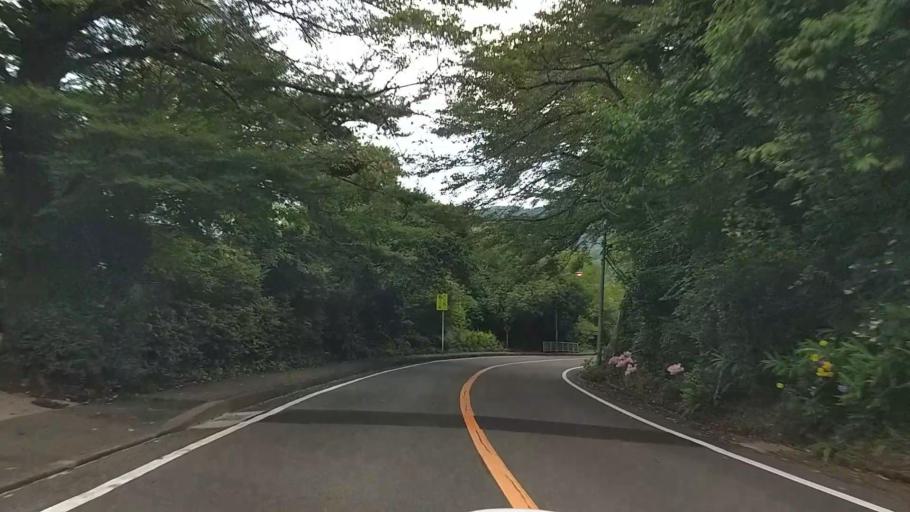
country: JP
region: Yamanashi
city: Uenohara
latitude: 35.6089
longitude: 139.1521
